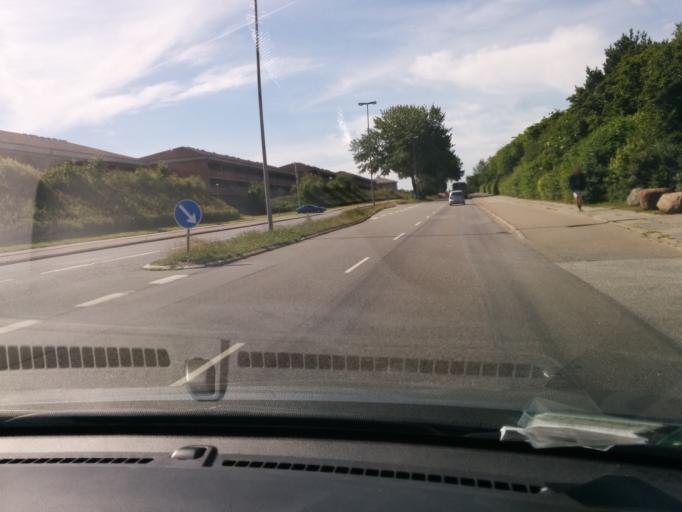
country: DK
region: Central Jutland
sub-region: Arhus Kommune
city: Arhus
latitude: 56.1793
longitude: 10.1678
